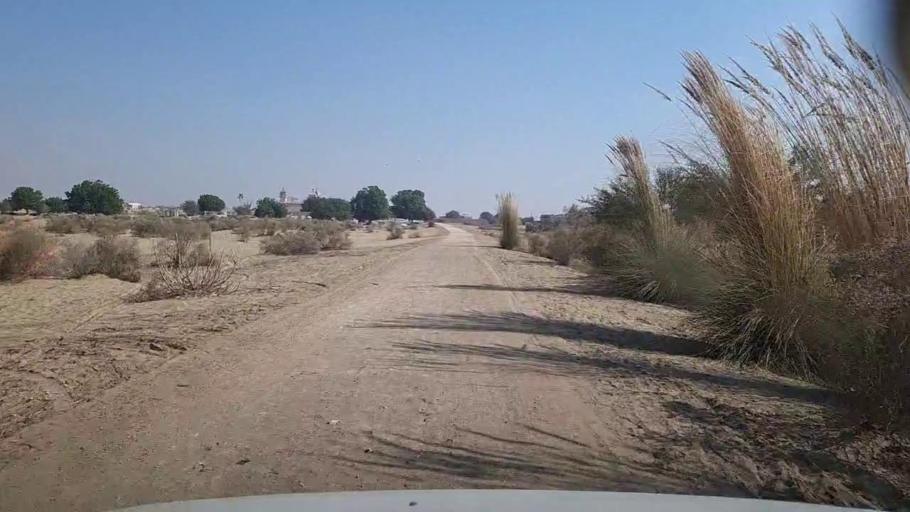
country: PK
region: Sindh
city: Khairpur
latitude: 28.0036
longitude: 69.8516
